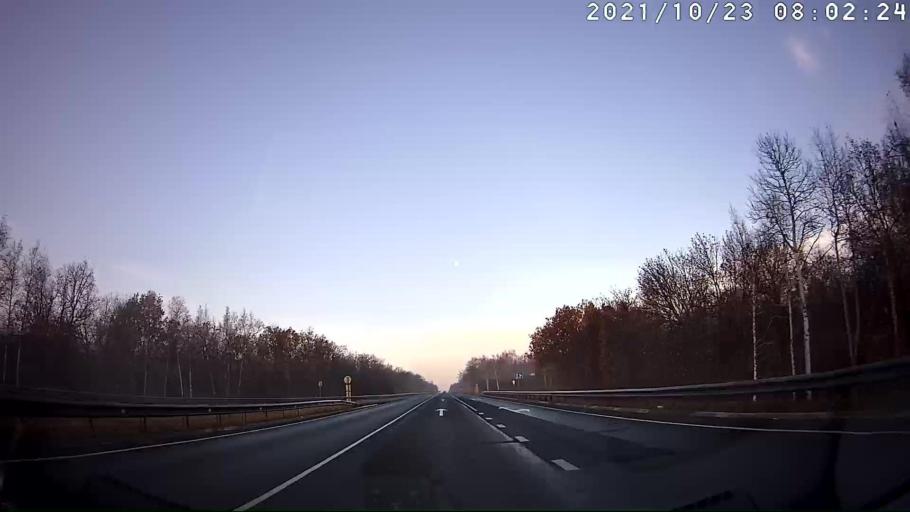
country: RU
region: Saratov
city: Vol'sk
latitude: 52.1091
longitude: 47.3789
